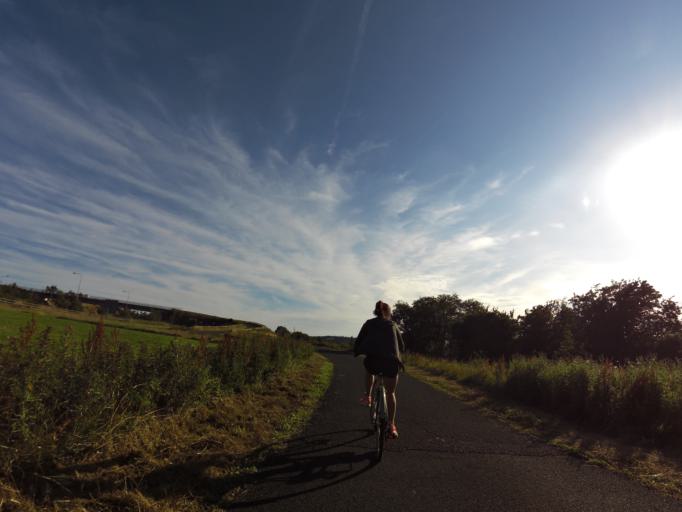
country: IE
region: Leinster
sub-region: Kilkenny
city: Mooncoin
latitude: 52.2576
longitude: -7.1879
